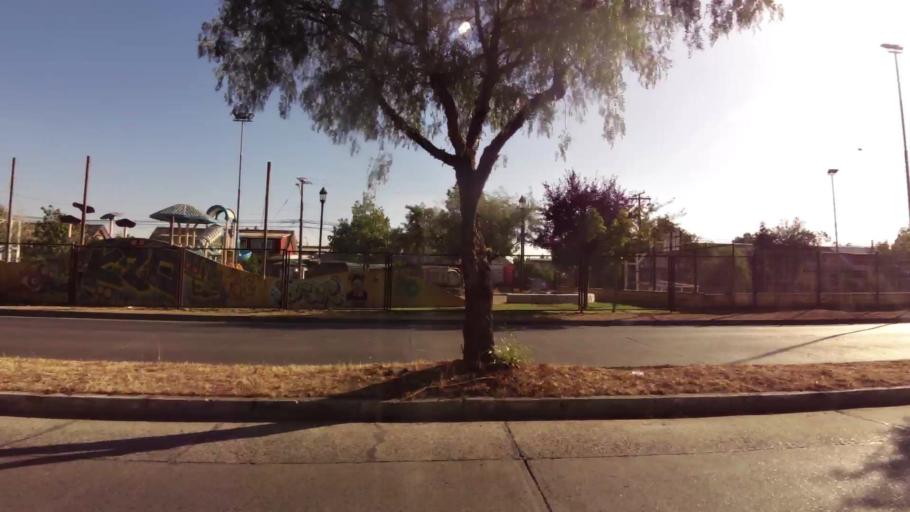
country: CL
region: Maule
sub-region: Provincia de Talca
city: Talca
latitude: -35.4423
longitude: -71.6739
